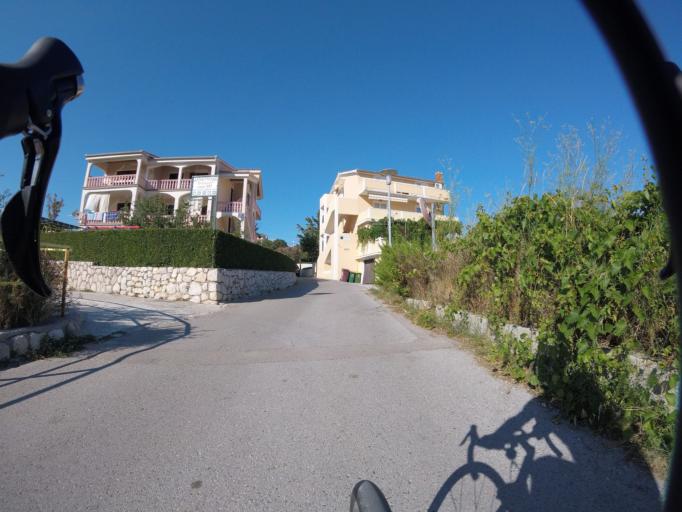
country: HR
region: Primorsko-Goranska
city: Lopar
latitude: 44.8325
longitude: 14.7333
